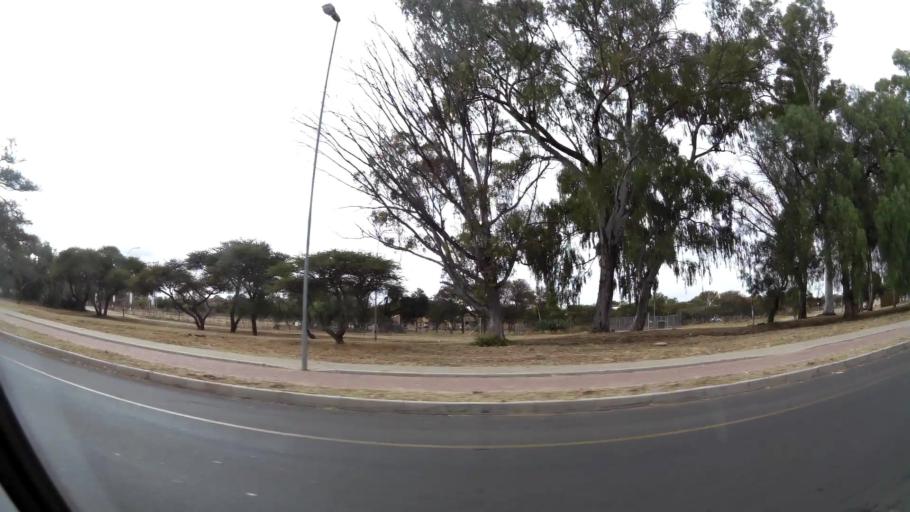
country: ZA
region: Limpopo
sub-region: Capricorn District Municipality
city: Polokwane
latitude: -23.9244
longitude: 29.4519
